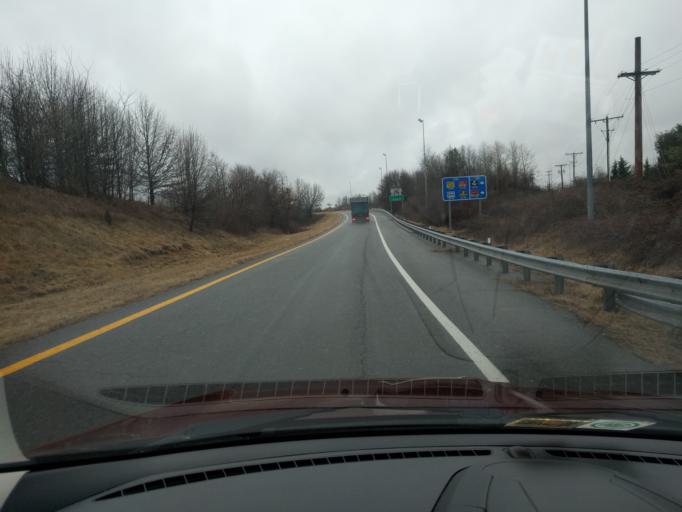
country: US
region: Virginia
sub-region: Montgomery County
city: Merrimac
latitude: 37.1666
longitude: -80.4158
